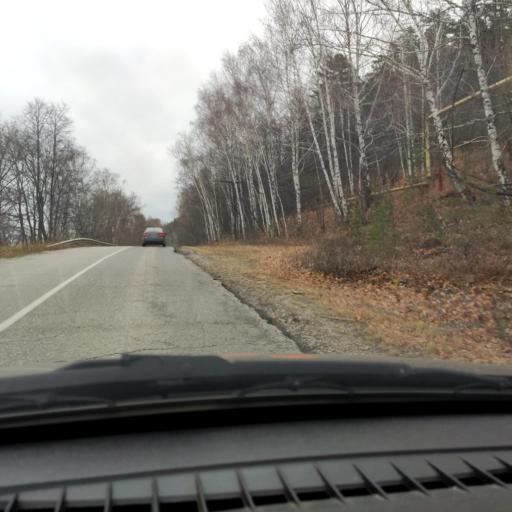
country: RU
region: Samara
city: Pribrezhnyy
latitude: 53.4395
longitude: 49.7419
